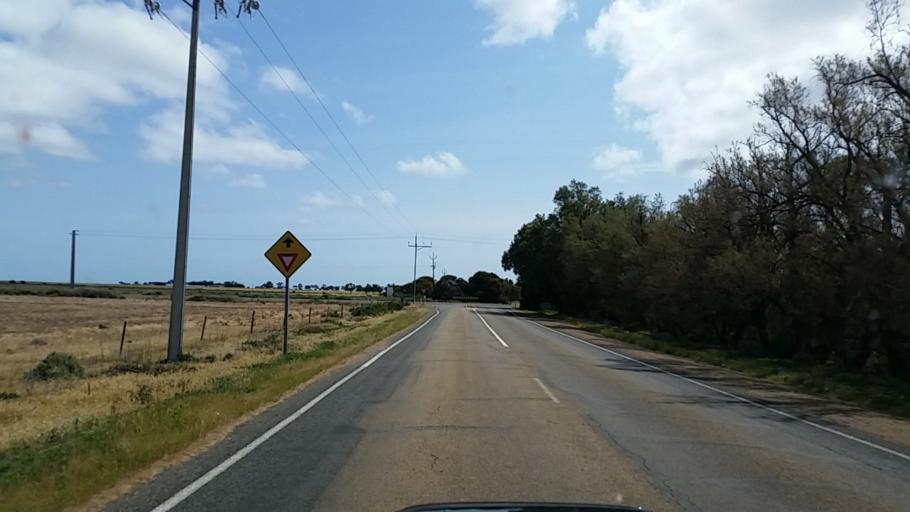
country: AU
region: South Australia
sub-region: Port Pirie City and Dists
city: Solomontown
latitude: -33.2301
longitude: 138.0151
